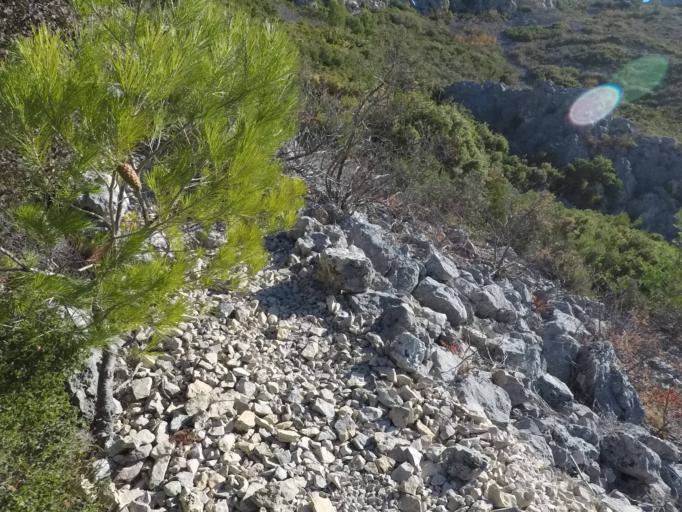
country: FR
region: Provence-Alpes-Cote d'Azur
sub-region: Departement des Bouches-du-Rhone
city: La Penne-sur-Huveaune
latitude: 43.2701
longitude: 5.4899
